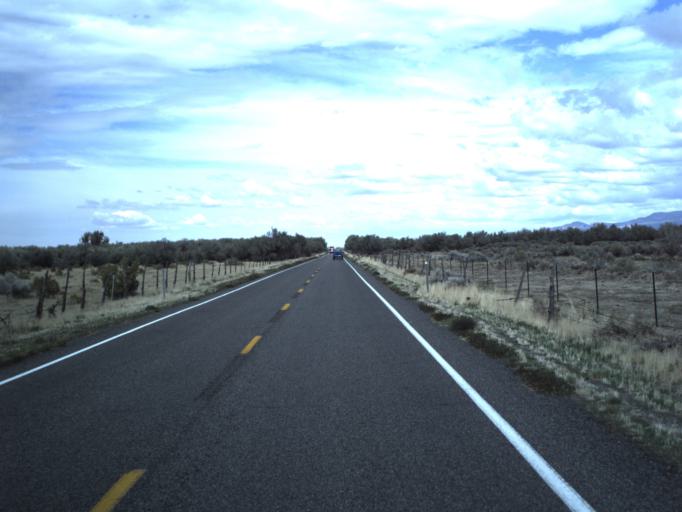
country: US
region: Utah
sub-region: Millard County
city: Fillmore
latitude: 39.0823
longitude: -112.4099
